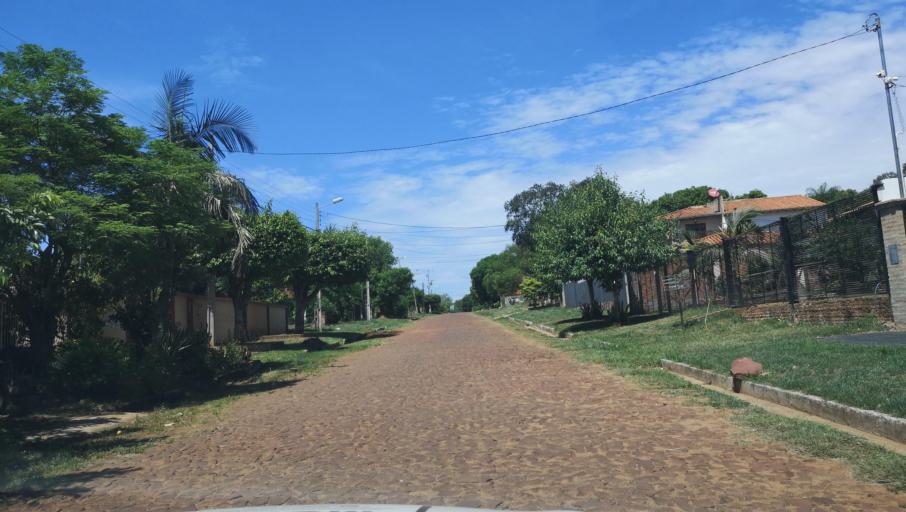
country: PY
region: Misiones
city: Santa Maria
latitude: -26.8761
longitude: -57.0304
